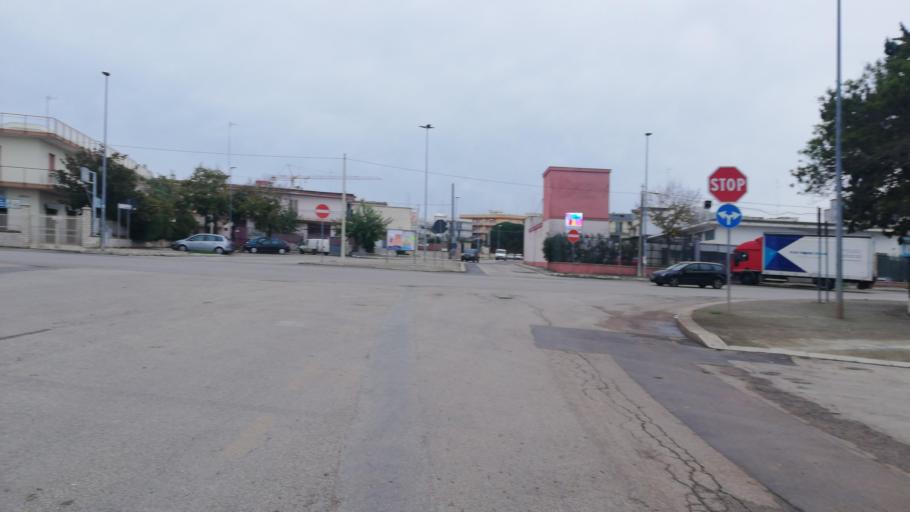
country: IT
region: Apulia
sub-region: Provincia di Bari
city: Bitonto
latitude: 41.1152
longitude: 16.6831
